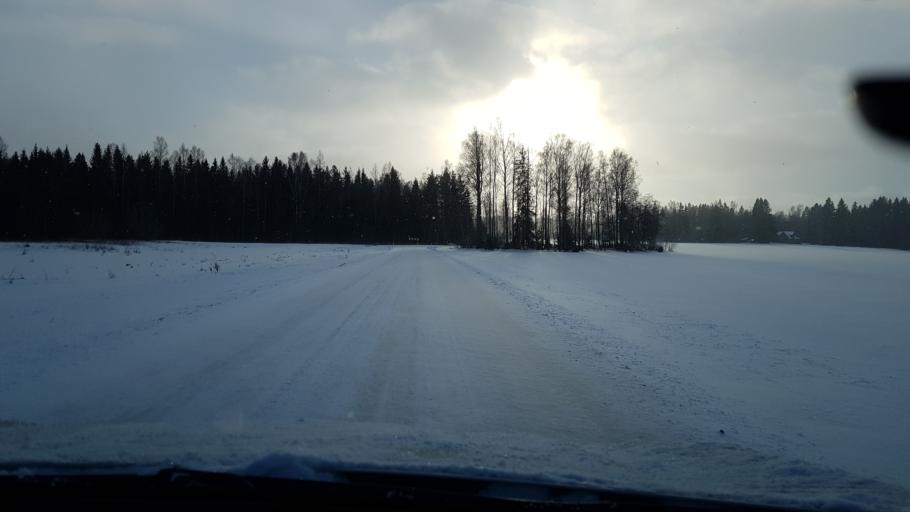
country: EE
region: Harju
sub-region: Nissi vald
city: Turba
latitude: 59.1996
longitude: 24.1397
